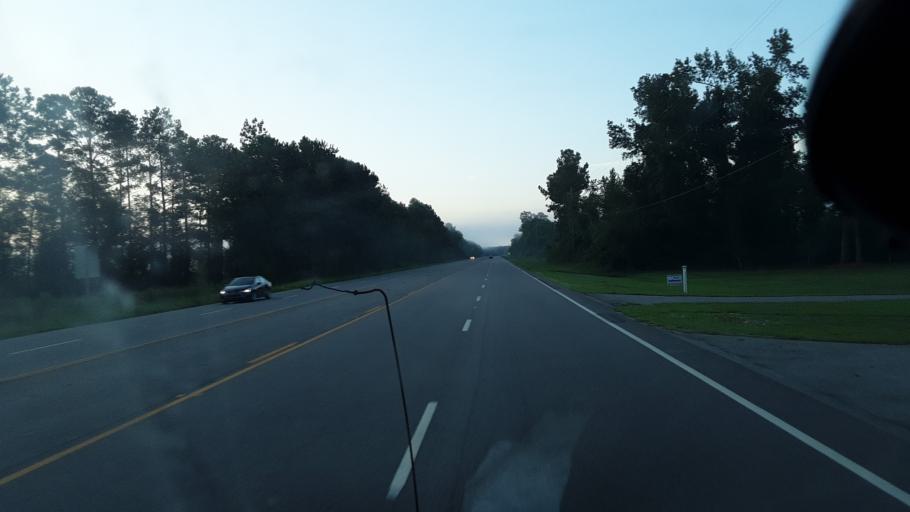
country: US
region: South Carolina
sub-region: Clarendon County
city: Manning
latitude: 33.7335
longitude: -80.2040
